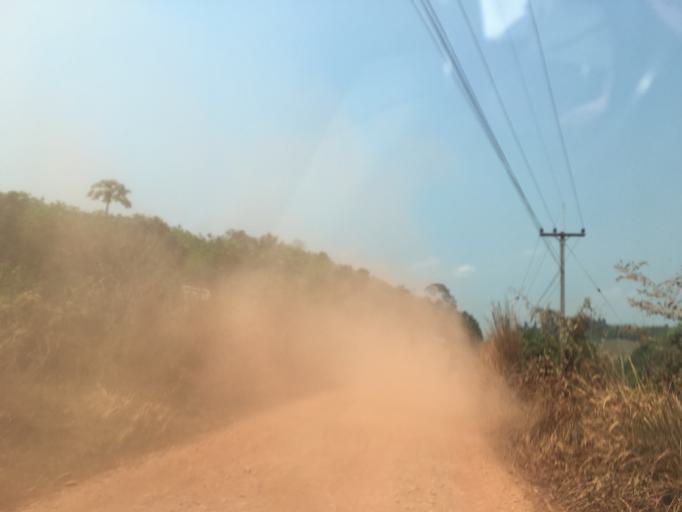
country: LA
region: Bolikhamxai
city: Bolikhan
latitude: 18.7462
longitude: 103.6162
